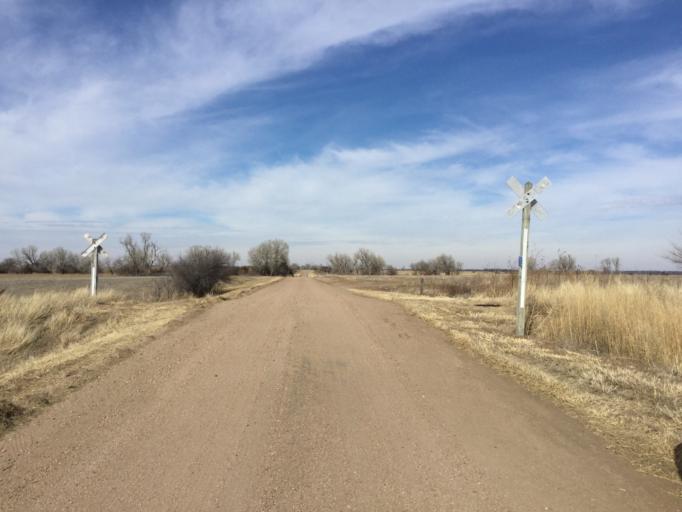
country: US
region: Kansas
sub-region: Rice County
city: Lyons
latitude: 38.3515
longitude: -98.3311
